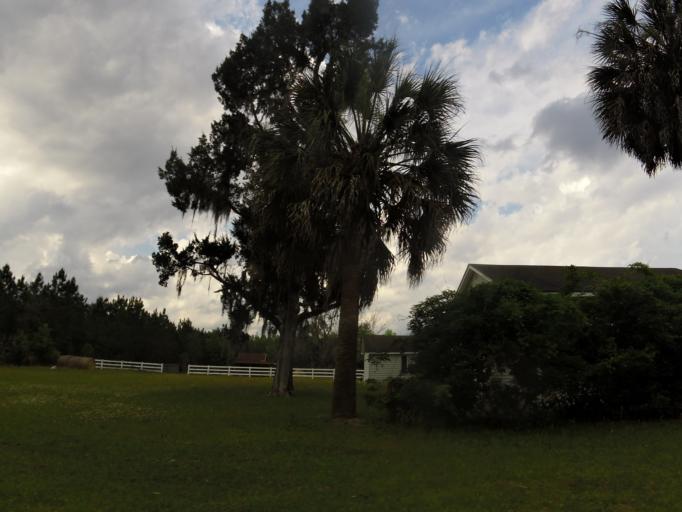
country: US
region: Georgia
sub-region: Charlton County
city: Folkston
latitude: 30.8215
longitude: -82.0646
